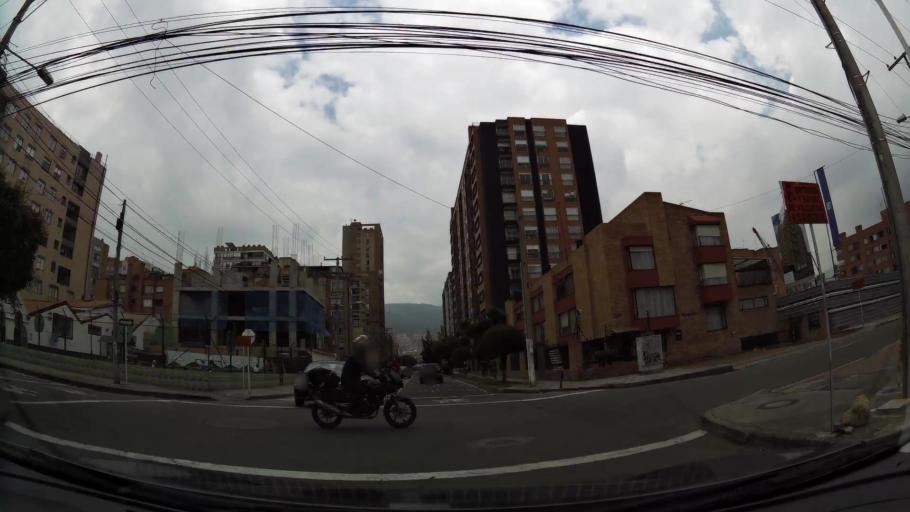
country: CO
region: Bogota D.C.
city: Barrio San Luis
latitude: 4.7258
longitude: -74.0379
